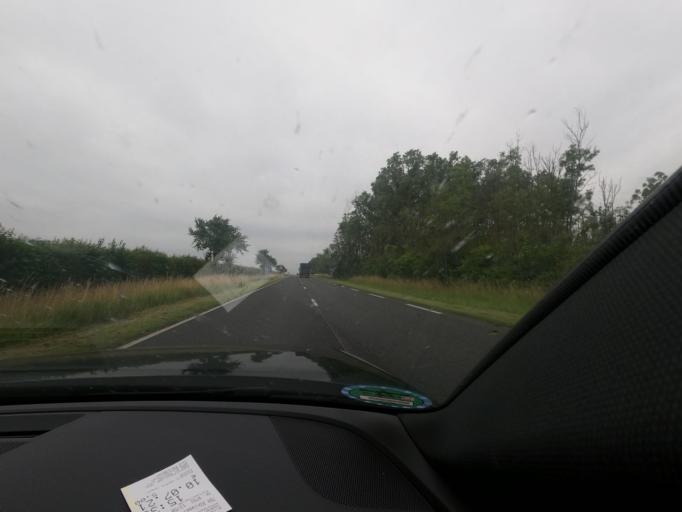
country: FR
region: Picardie
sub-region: Departement de la Somme
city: Harbonnieres
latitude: 49.7831
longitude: 2.5874
